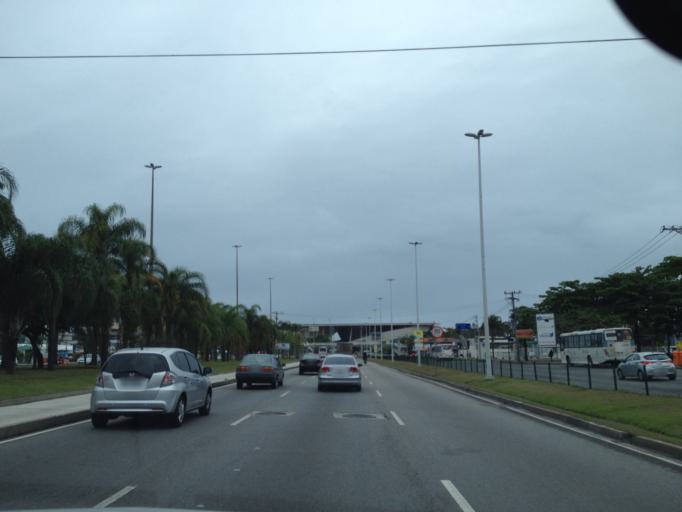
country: BR
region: Rio de Janeiro
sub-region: Rio De Janeiro
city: Rio de Janeiro
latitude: -22.9923
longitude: -43.3661
